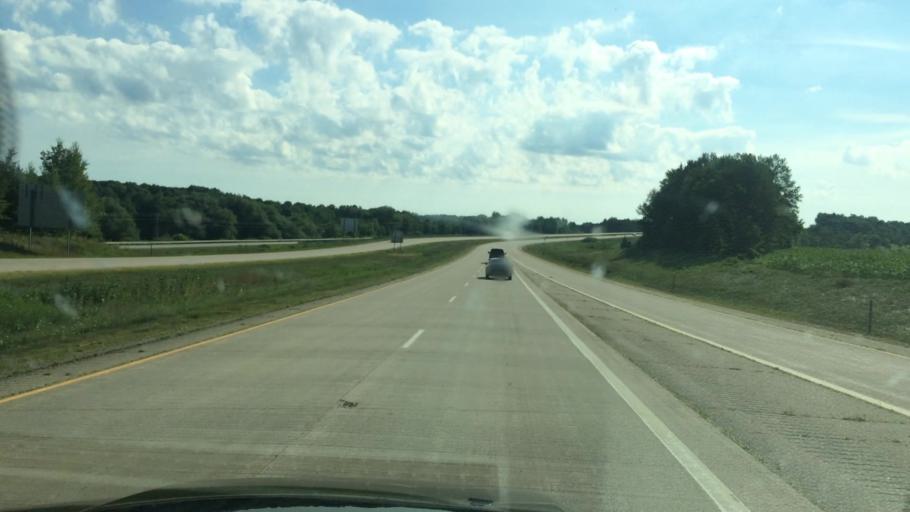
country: US
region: Wisconsin
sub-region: Shawano County
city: Wittenberg
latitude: 44.8247
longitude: -89.1176
